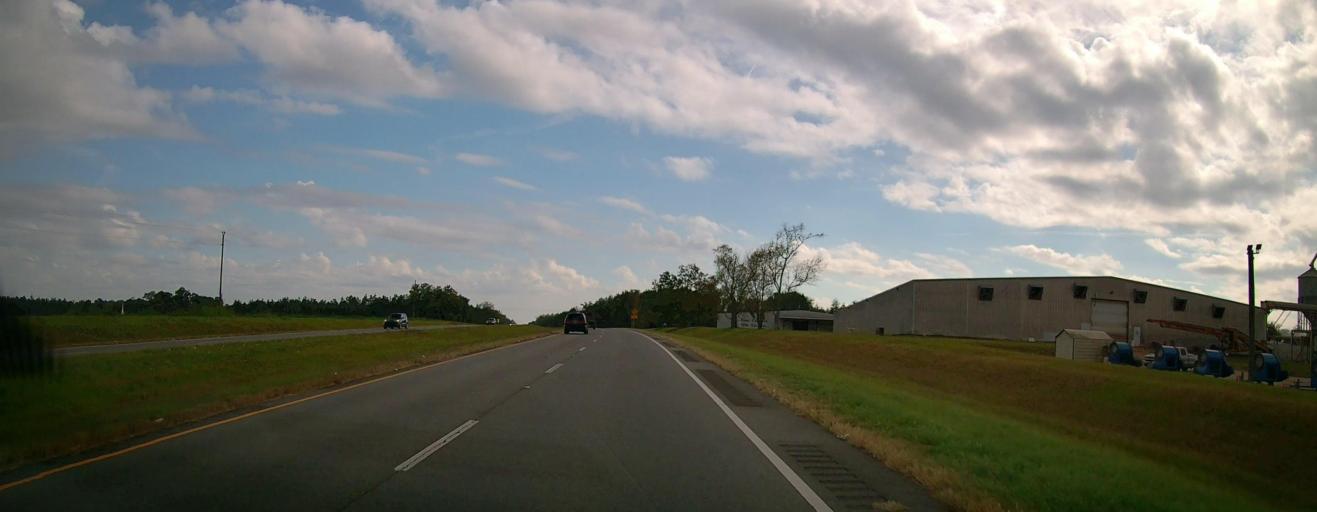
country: US
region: Georgia
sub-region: Thomas County
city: Meigs
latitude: 31.0472
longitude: -84.0705
